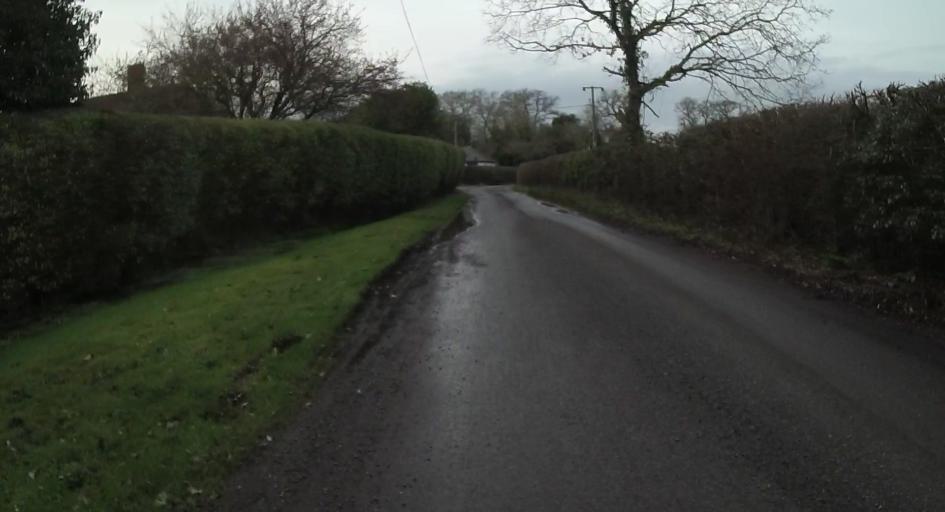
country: GB
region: England
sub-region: Hampshire
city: Tadley
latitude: 51.3608
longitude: -1.0860
